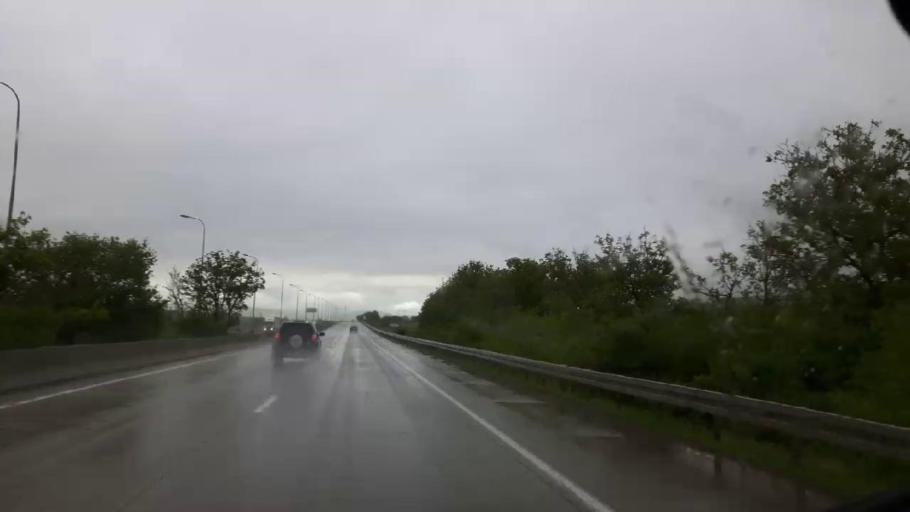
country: GE
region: Shida Kartli
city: Kaspi
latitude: 42.0199
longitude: 44.3090
